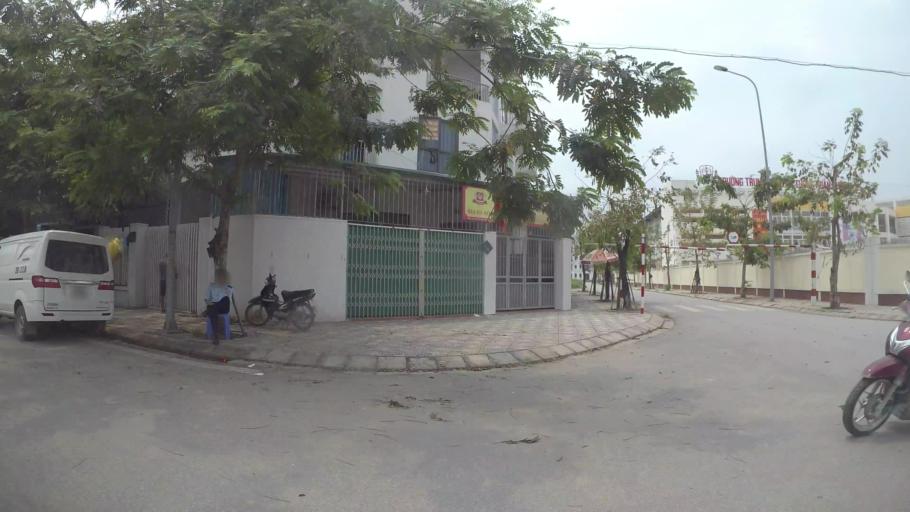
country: VN
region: Ha Noi
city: Cau Dien
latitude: 21.0313
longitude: 105.7478
